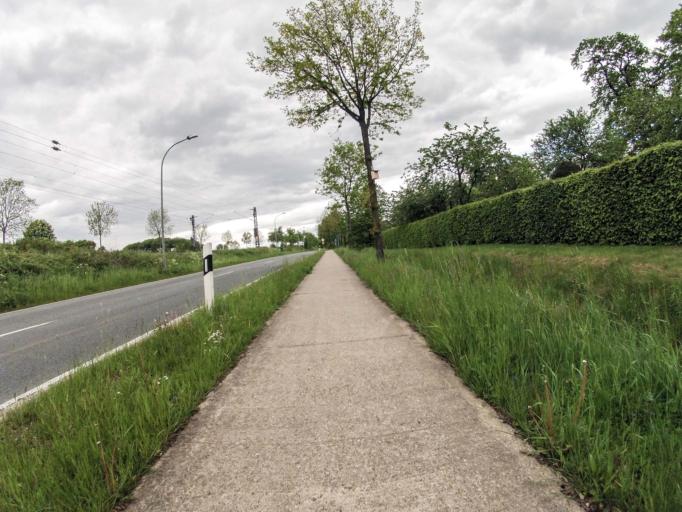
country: DE
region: Lower Saxony
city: Belm
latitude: 52.3293
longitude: 8.1464
